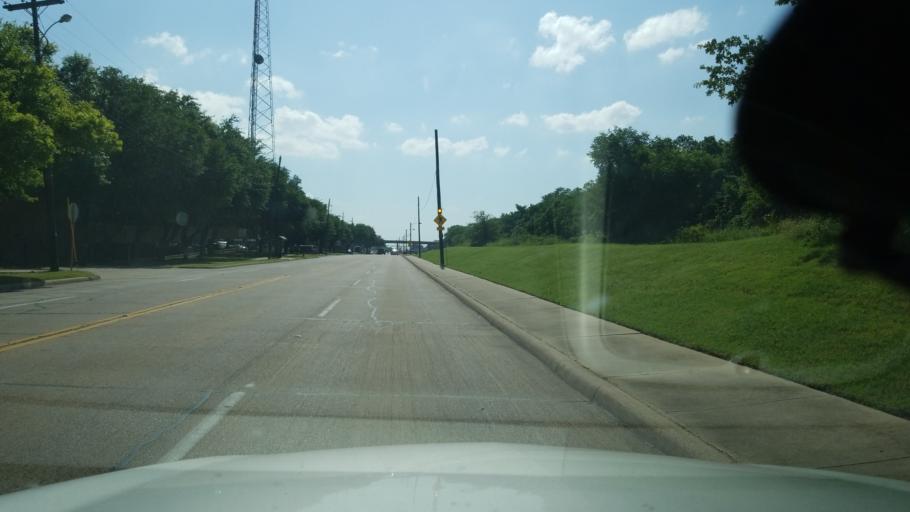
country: US
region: Texas
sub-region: Dallas County
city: Irving
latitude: 32.8151
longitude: -96.9544
